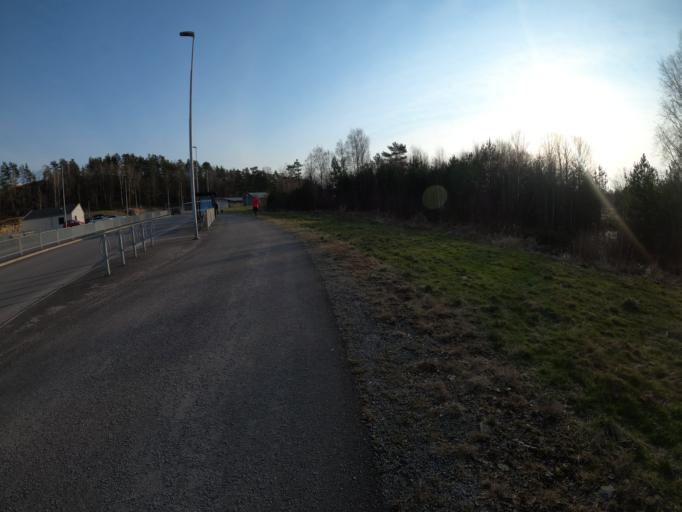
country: SE
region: Vaestra Goetaland
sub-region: Harryda Kommun
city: Molnlycke
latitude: 57.6537
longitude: 12.1283
